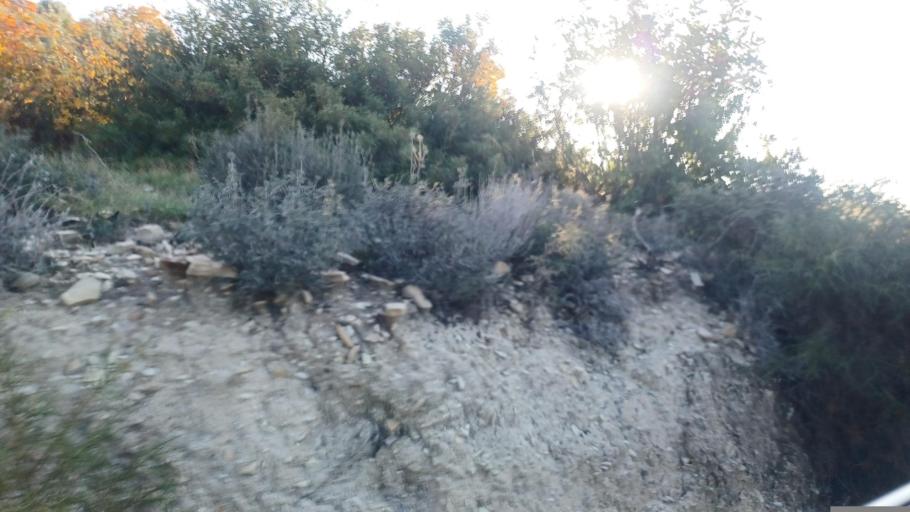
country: CY
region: Larnaka
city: Kofinou
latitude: 34.8241
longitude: 33.3100
